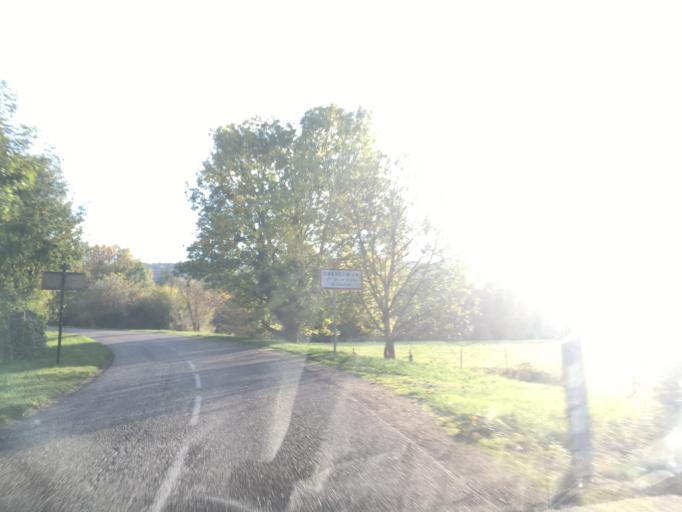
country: FR
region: Haute-Normandie
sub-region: Departement de l'Eure
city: Heudreville-sur-Eure
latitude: 49.1041
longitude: 1.2409
